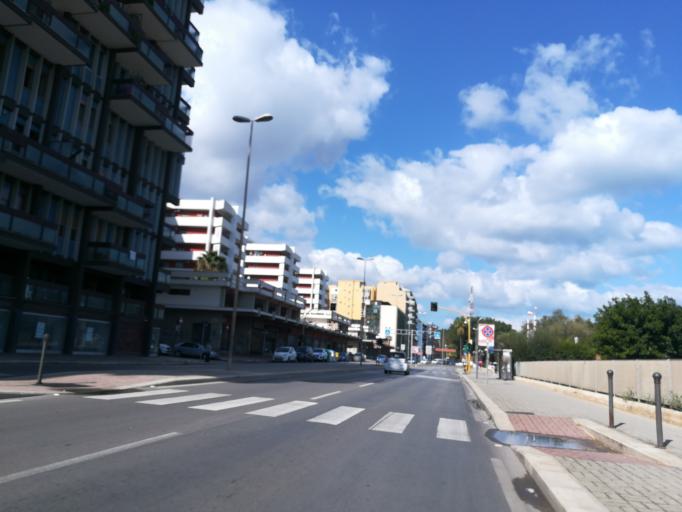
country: IT
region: Apulia
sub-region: Provincia di Bari
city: Bari
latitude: 41.1173
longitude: 16.8930
